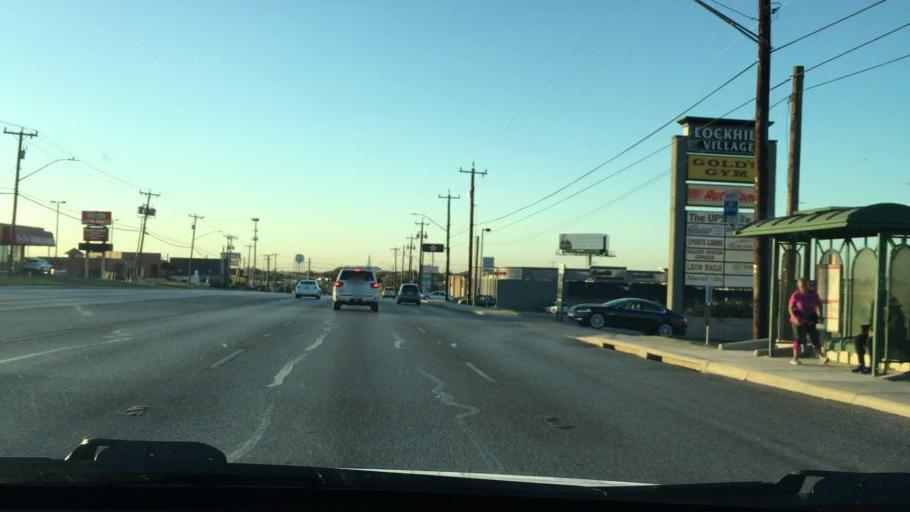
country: US
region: Texas
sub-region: Bexar County
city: Castle Hills
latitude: 29.5440
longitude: -98.5291
